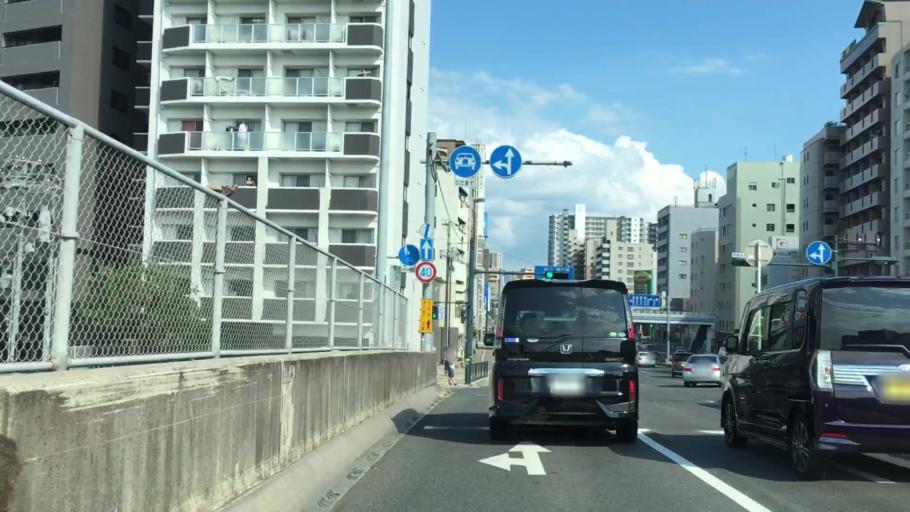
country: JP
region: Hiroshima
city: Hiroshima-shi
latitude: 34.3872
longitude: 132.4407
